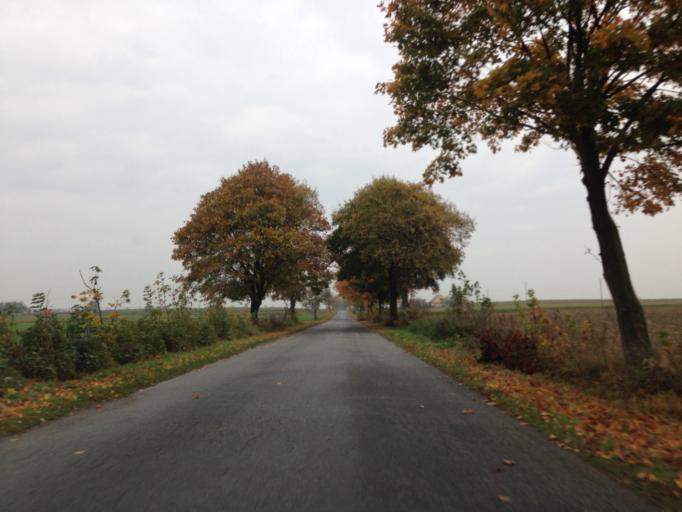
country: PL
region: Kujawsko-Pomorskie
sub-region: Powiat rypinski
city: Rypin
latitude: 53.1213
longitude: 19.4027
